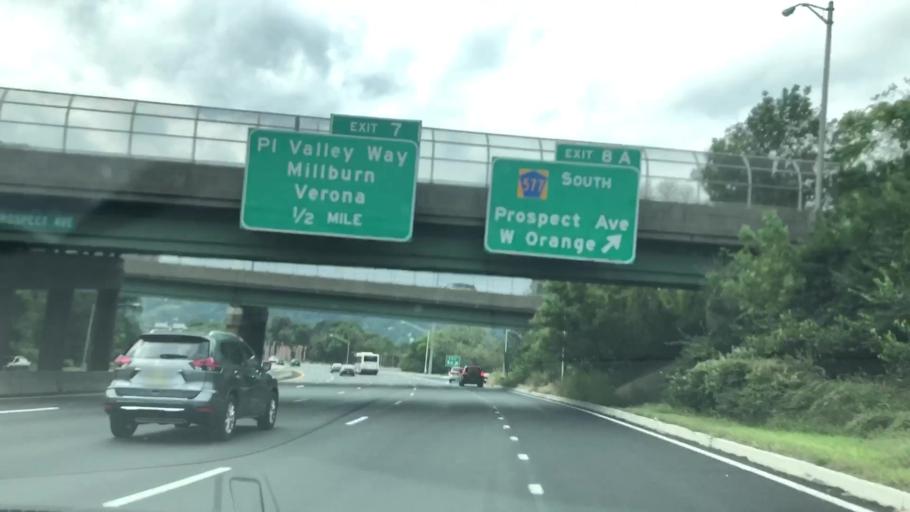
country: US
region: New Jersey
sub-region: Essex County
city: West Orange
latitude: 40.7975
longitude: -74.2519
